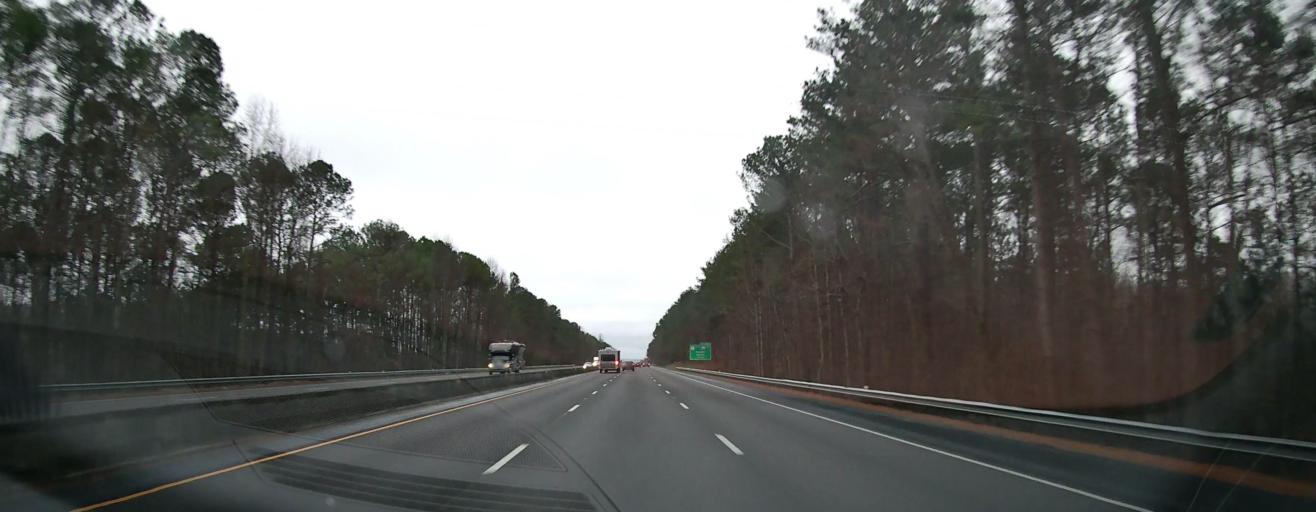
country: US
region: Alabama
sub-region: Blount County
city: Smoke Rise
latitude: 33.8643
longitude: -86.8331
